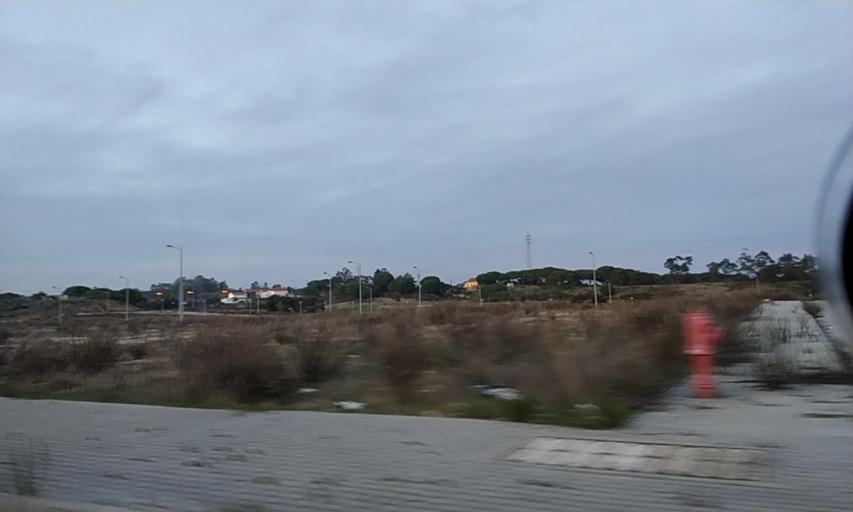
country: PT
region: Setubal
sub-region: Setubal
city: Setubal
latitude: 38.5146
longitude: -8.8547
